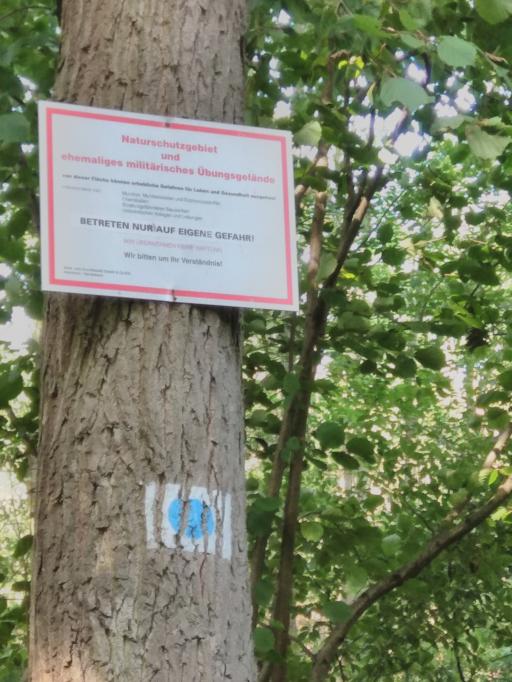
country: DE
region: Brandenburg
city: Baruth
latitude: 52.1230
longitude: 13.5267
